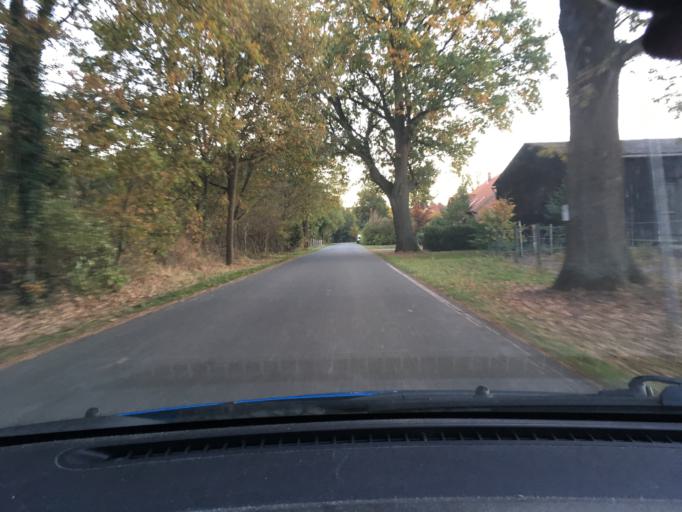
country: DE
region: Lower Saxony
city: Neetze
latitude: 53.2965
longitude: 10.6163
